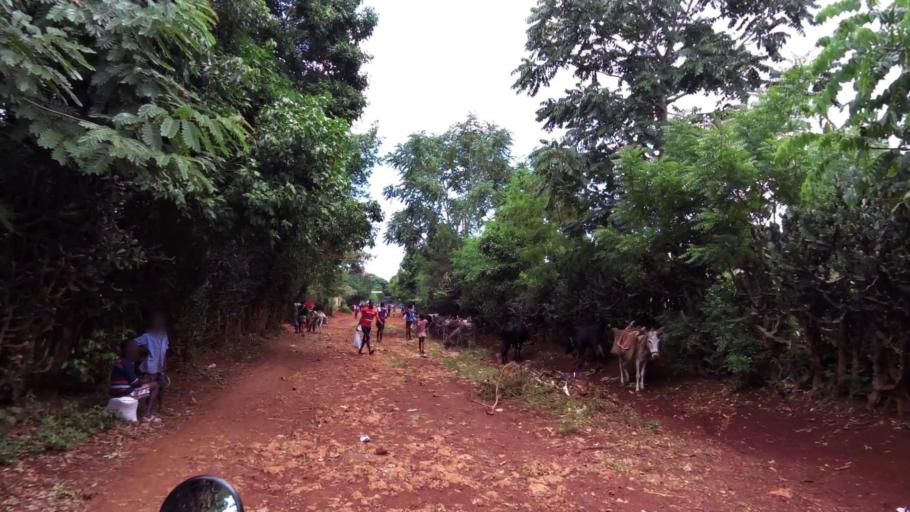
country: HT
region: Ouest
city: Anse a Galets
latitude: 18.7796
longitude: -72.8620
